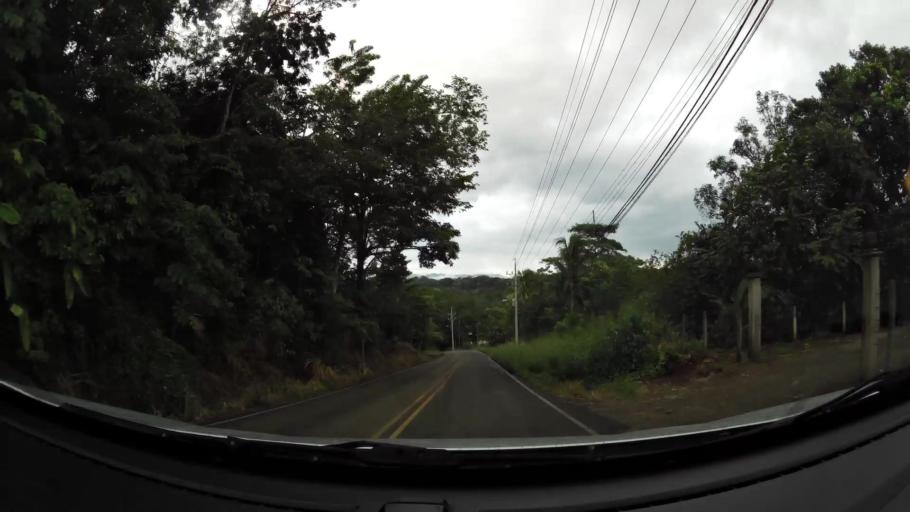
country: CR
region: Puntarenas
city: Esparza
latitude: 9.9616
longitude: -84.6100
